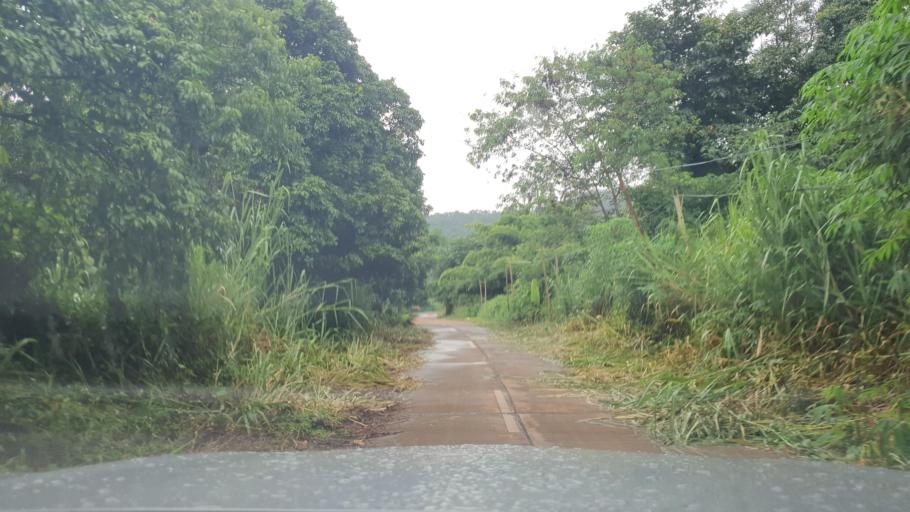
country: TH
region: Chiang Mai
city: Samoeng
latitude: 18.8300
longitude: 98.7708
